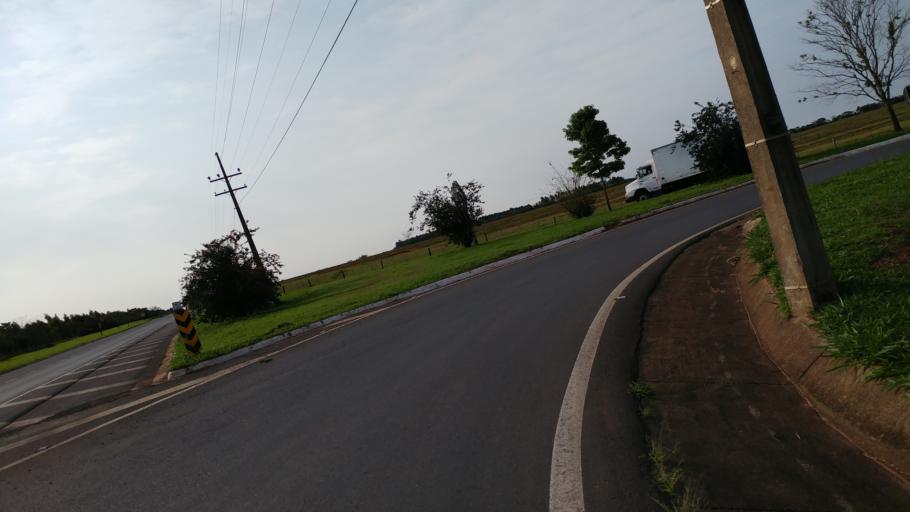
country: BR
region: Sao Paulo
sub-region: Paraguacu Paulista
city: Paraguacu Paulista
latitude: -22.4092
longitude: -50.5979
